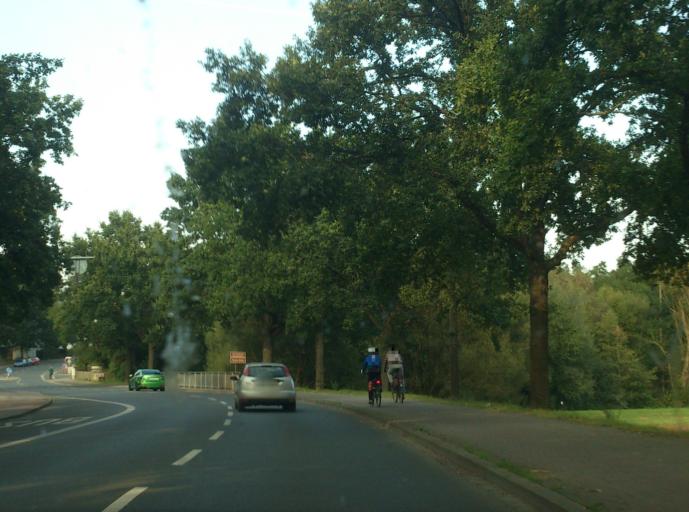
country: DE
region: Bavaria
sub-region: Regierungsbezirk Mittelfranken
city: Buckenhof
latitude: 49.5979
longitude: 11.0368
